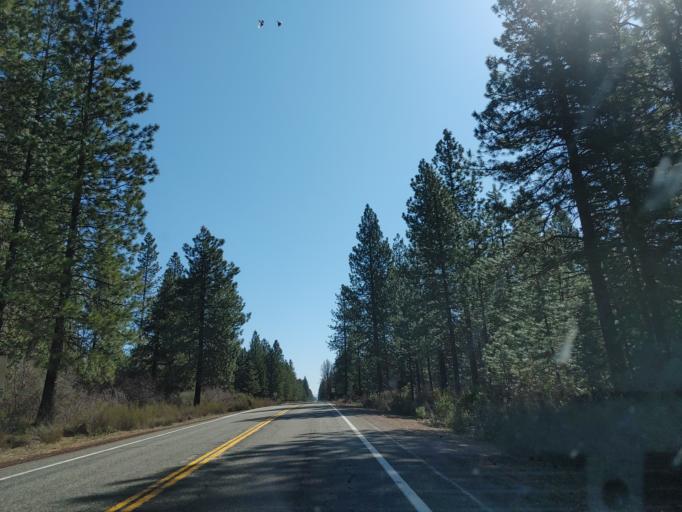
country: US
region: California
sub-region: Siskiyou County
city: McCloud
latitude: 41.2514
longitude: -122.1219
